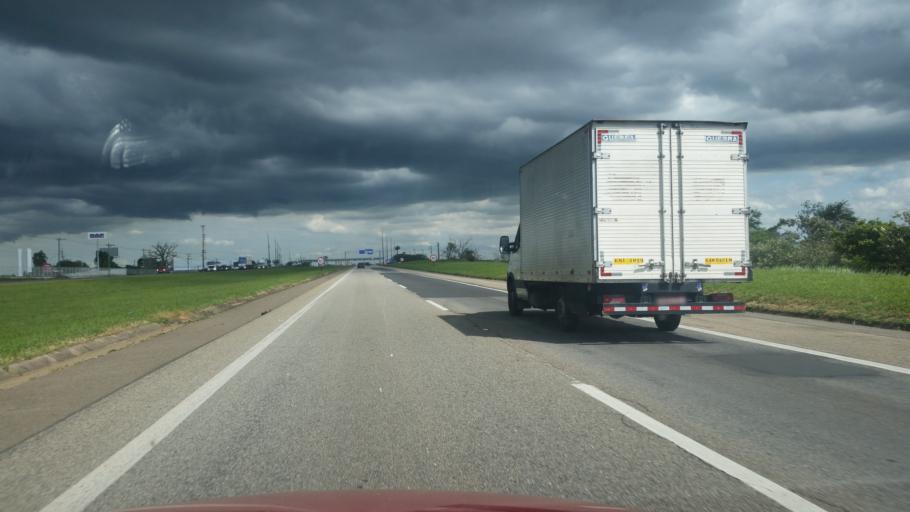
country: BR
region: Sao Paulo
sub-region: Boituva
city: Boituva
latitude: -23.3099
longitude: -47.6498
